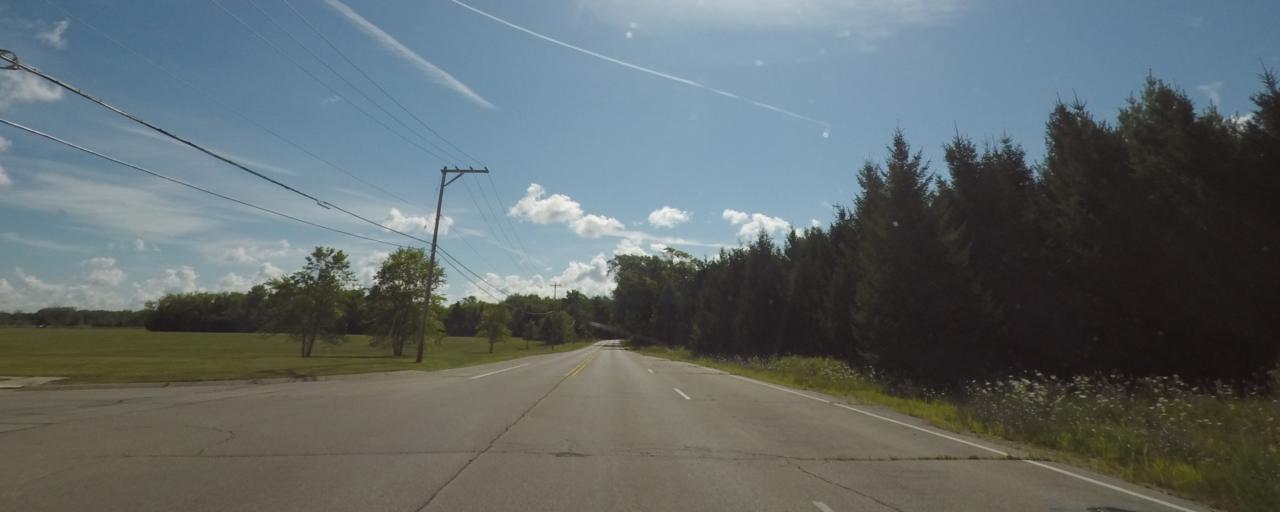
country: US
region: Wisconsin
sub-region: Waukesha County
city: Oconomowoc
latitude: 43.0848
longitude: -88.5140
